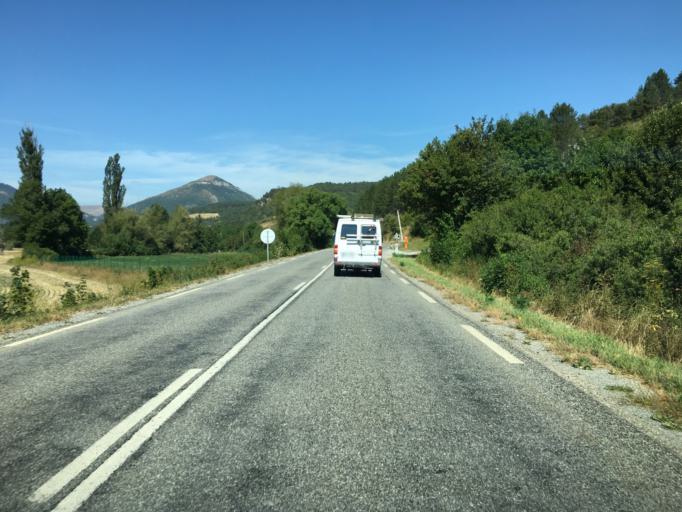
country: FR
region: Provence-Alpes-Cote d'Azur
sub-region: Departement des Hautes-Alpes
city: Veynes
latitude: 44.5635
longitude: 5.7610
